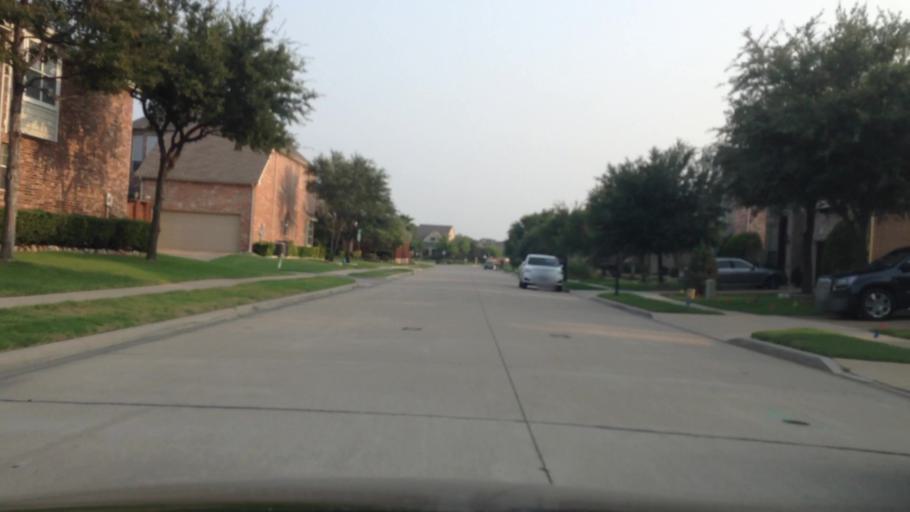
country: US
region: Texas
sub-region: Collin County
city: Frisco
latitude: 33.1258
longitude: -96.8463
